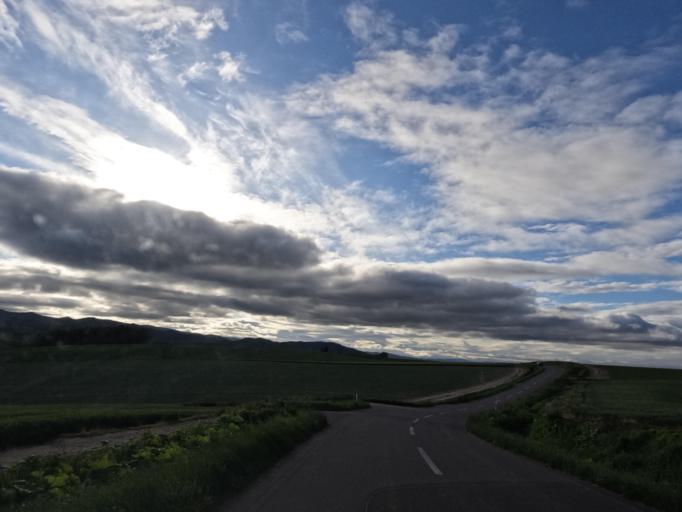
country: JP
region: Hokkaido
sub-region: Asahikawa-shi
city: Asahikawa
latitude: 43.6242
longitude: 142.4386
